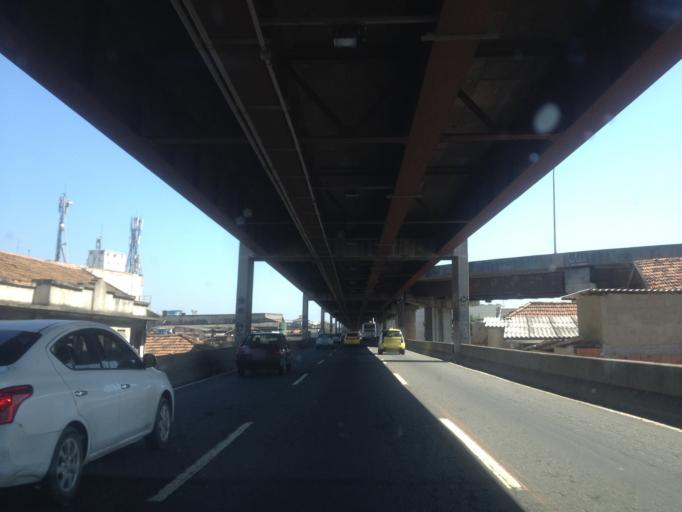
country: BR
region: Rio de Janeiro
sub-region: Rio De Janeiro
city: Rio de Janeiro
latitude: -22.8912
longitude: -43.2230
